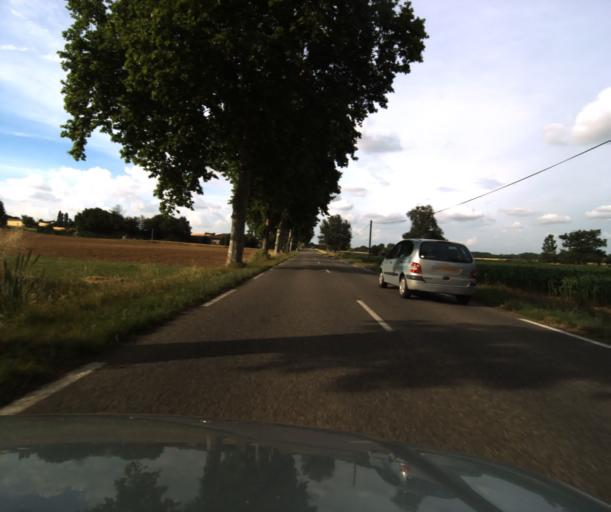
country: FR
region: Midi-Pyrenees
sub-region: Departement du Tarn-et-Garonne
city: Beaumont-de-Lomagne
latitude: 43.8353
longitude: 0.9247
